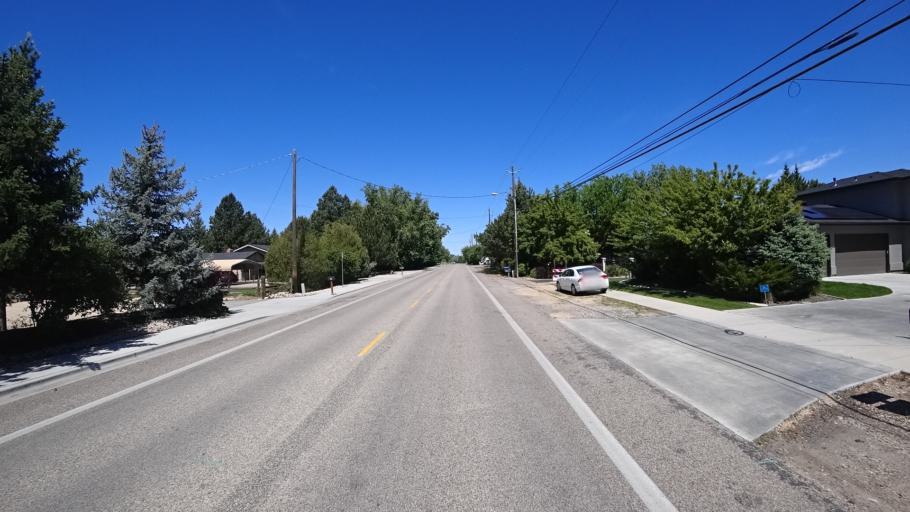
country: US
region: Idaho
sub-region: Ada County
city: Boise
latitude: 43.5701
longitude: -116.1515
